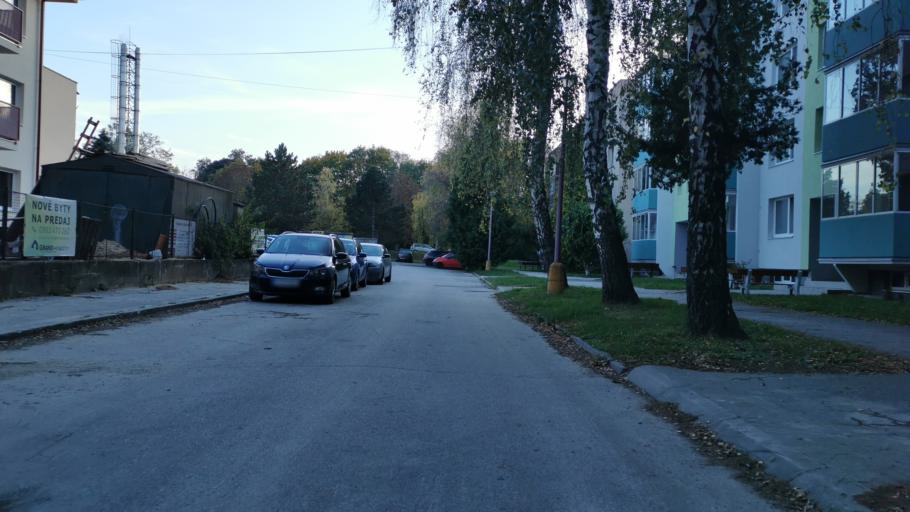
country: SK
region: Trnavsky
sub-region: Okres Skalica
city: Skalica
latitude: 48.8380
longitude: 17.2344
